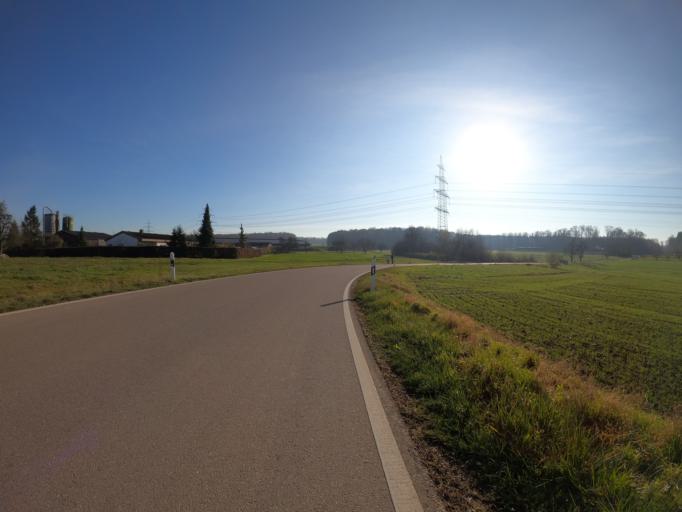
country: DE
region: Baden-Wuerttemberg
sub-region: Regierungsbezirk Stuttgart
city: Ebersbach an der Fils
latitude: 48.7044
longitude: 9.5420
